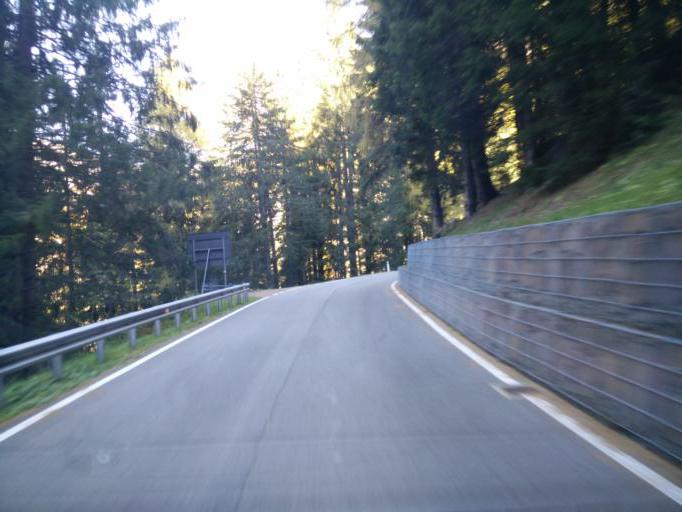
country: IT
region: Trentino-Alto Adige
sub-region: Bolzano
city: Moso in Passiria
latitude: 46.8574
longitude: 11.1622
